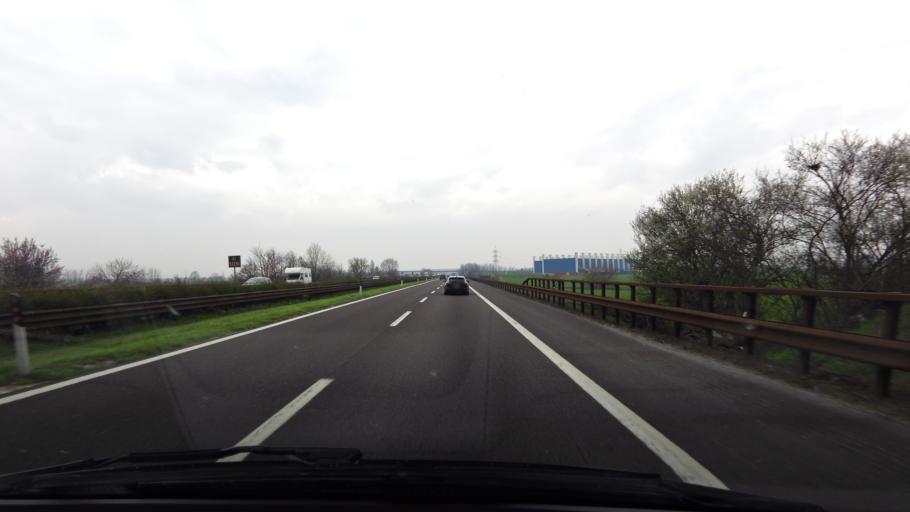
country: IT
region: Lombardy
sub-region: Provincia di Mantova
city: Stradella
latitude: 45.1476
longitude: 10.8670
